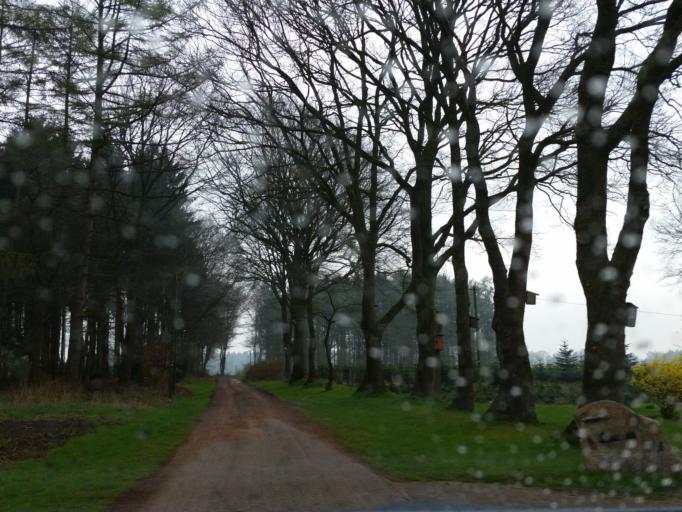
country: DE
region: Lower Saxony
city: Hipstedt
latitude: 53.5674
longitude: 8.9789
